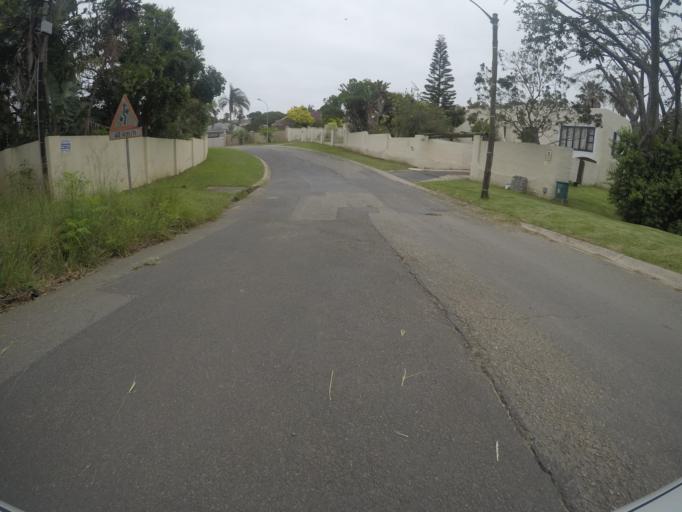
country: ZA
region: Eastern Cape
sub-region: Buffalo City Metropolitan Municipality
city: East London
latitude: -32.9782
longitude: 27.9398
